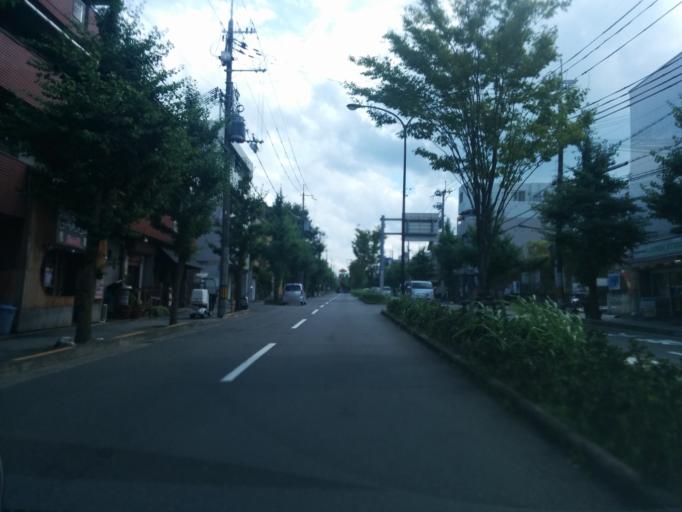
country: JP
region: Kyoto
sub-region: Kyoto-shi
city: Kamigyo-ku
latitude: 35.0485
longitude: 135.7408
